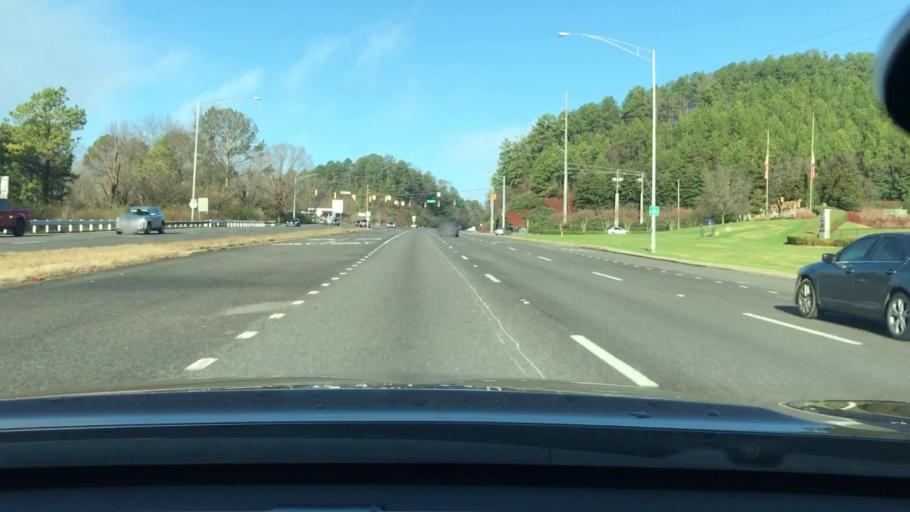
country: US
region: Alabama
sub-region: Jefferson County
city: Cahaba Heights
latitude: 33.4442
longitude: -86.7334
